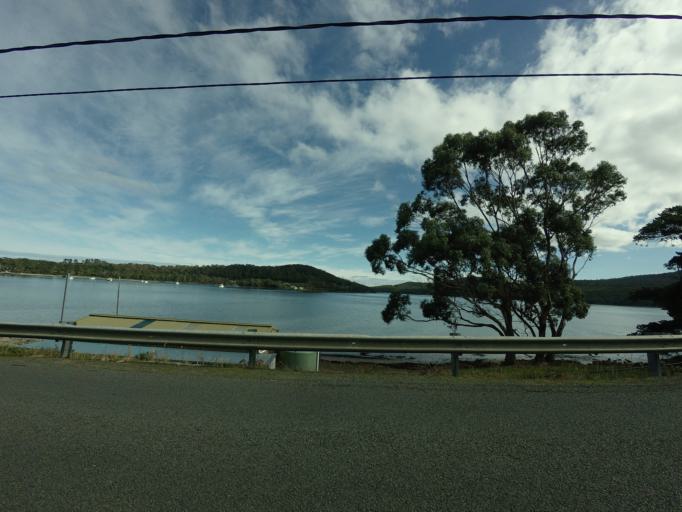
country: AU
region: Tasmania
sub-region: Clarence
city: Sandford
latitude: -43.0999
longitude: 147.7419
